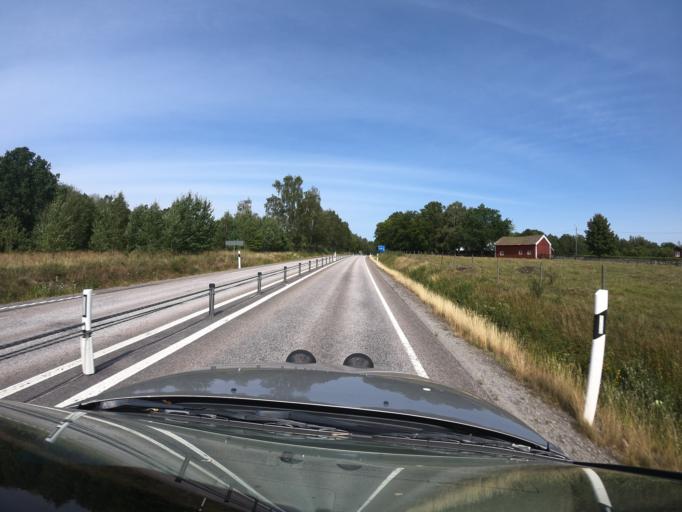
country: SE
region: Kronoberg
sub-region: Vaxjo Kommun
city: Rottne
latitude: 56.9827
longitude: 14.9851
